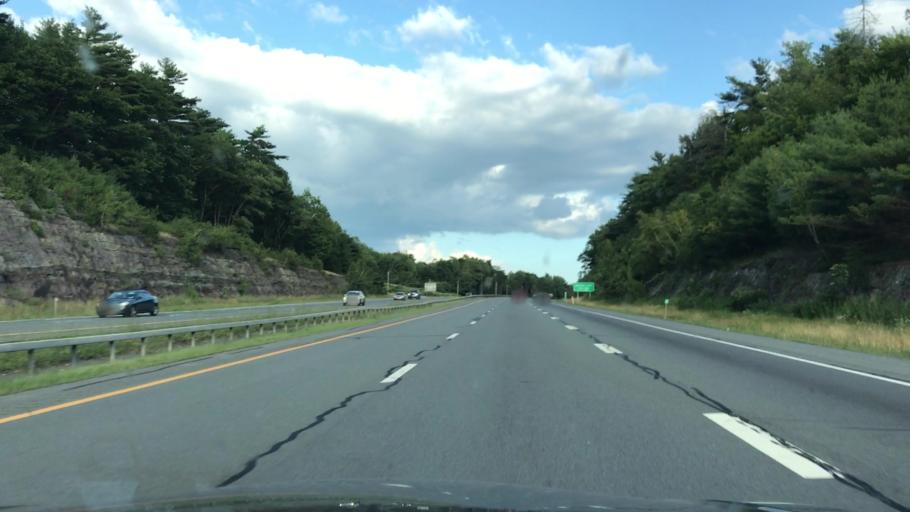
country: US
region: New York
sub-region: Sullivan County
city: Rock Hill
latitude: 41.6204
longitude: -74.5855
